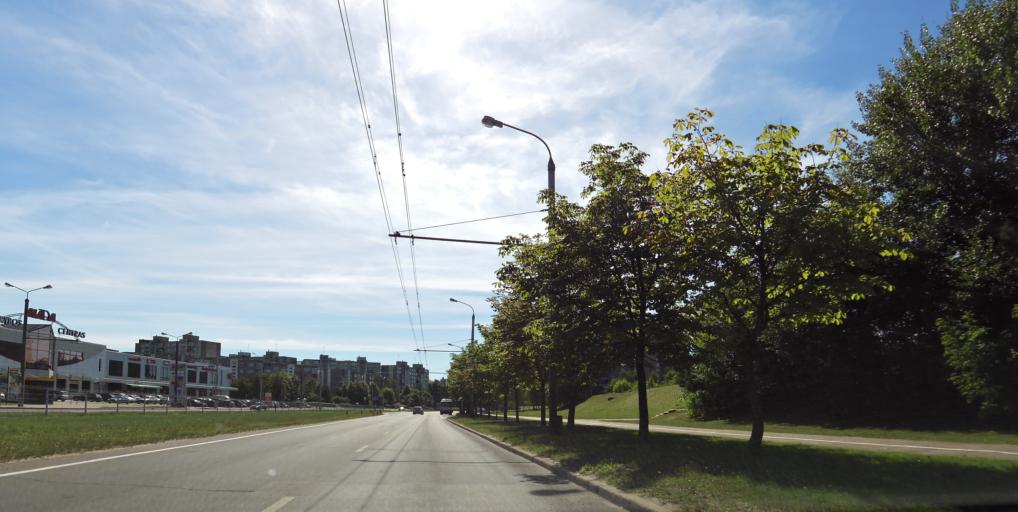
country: LT
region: Vilnius County
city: Justiniskes
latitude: 54.7088
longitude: 25.2261
